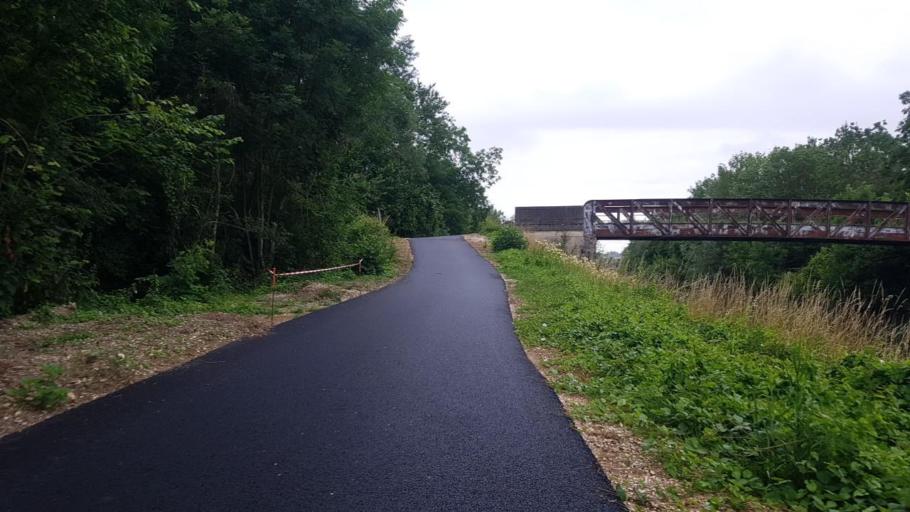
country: FR
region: Champagne-Ardenne
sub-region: Departement de la Marne
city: Vitry-le-Francois
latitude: 48.8260
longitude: 4.5149
